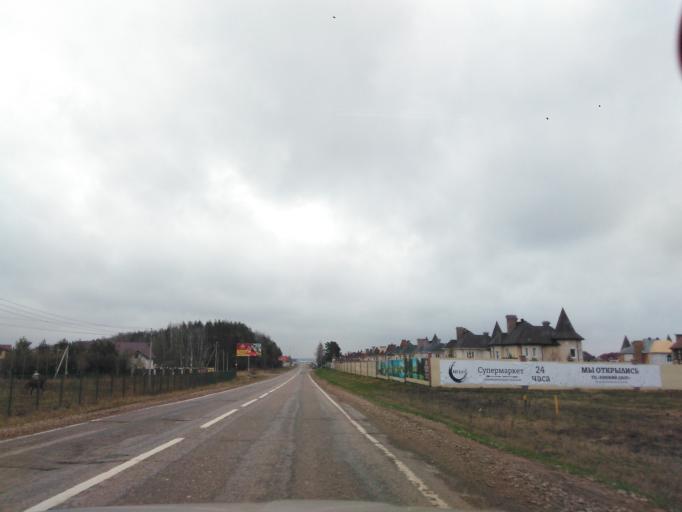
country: RU
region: Moskovskaya
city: Rozhdestveno
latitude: 55.8276
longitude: 37.0370
